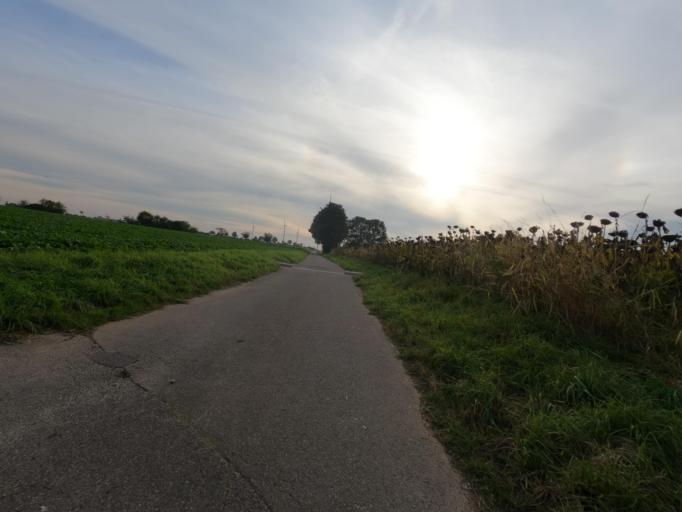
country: DE
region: North Rhine-Westphalia
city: Huckelhoven
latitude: 51.0338
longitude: 6.1688
